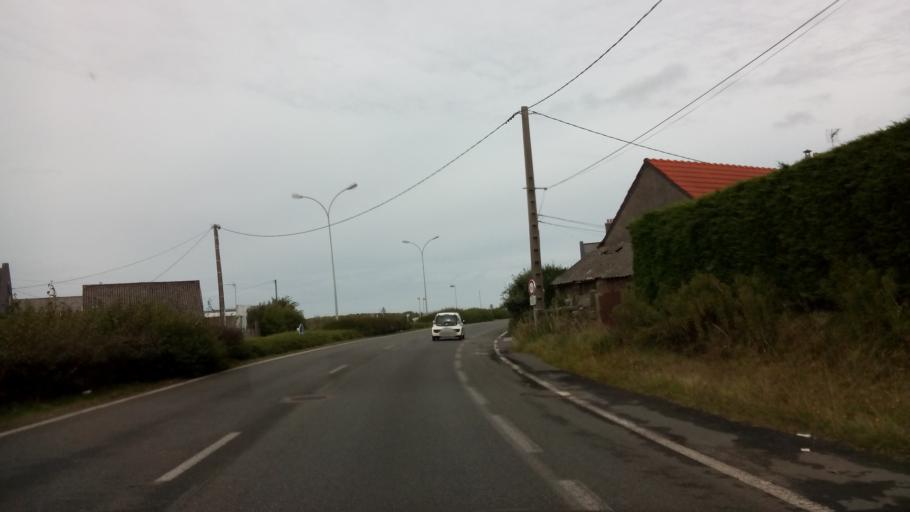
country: FR
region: Brittany
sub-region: Departement des Cotes-d'Armor
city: Lannion
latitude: 48.7494
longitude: -3.4608
